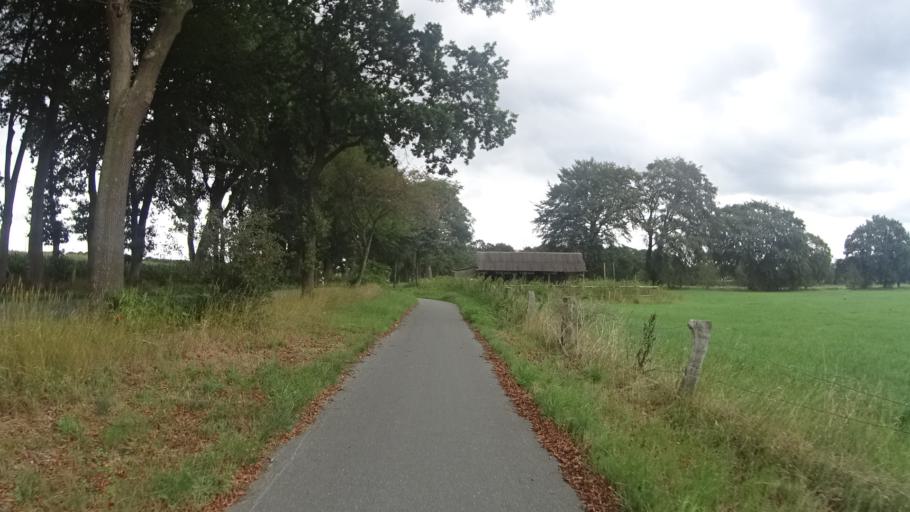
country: DE
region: Lower Saxony
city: Kuhrstedt
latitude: 53.5874
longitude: 8.8034
